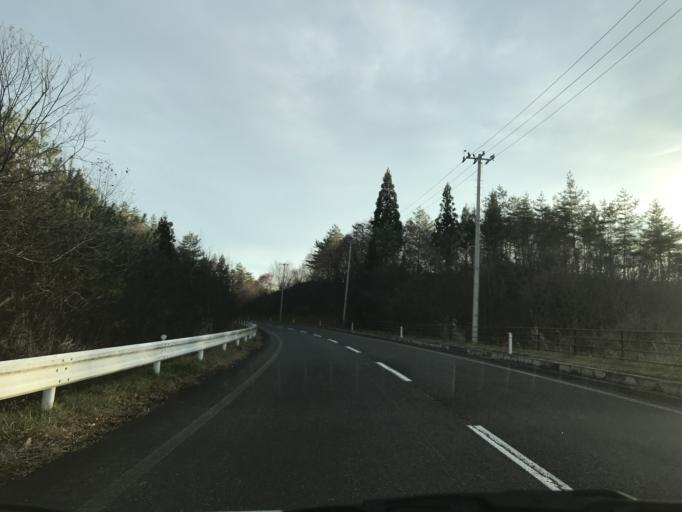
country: JP
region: Iwate
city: Ichinoseki
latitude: 38.9845
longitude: 141.0675
